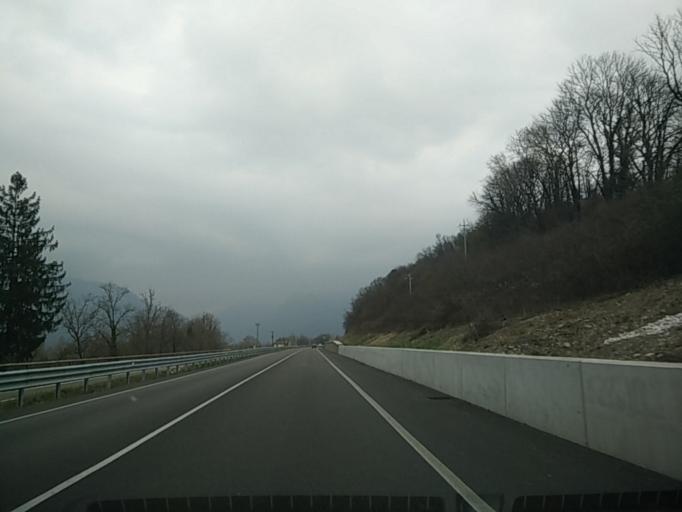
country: IT
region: Veneto
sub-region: Provincia di Belluno
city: Castion
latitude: 46.1369
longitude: 12.2311
